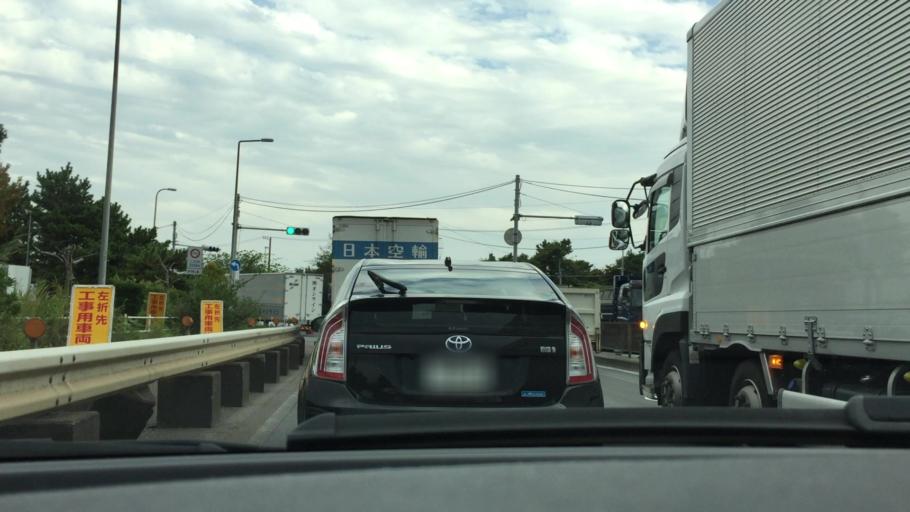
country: JP
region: Kanagawa
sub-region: Kawasaki-shi
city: Kawasaki
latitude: 35.5790
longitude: 139.7738
